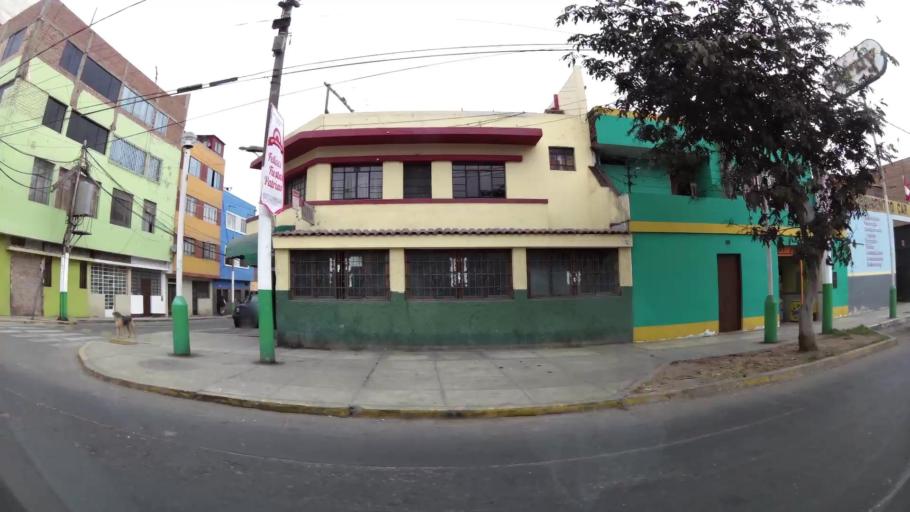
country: PE
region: Callao
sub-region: Callao
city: Callao
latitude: -12.0662
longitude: -77.1234
